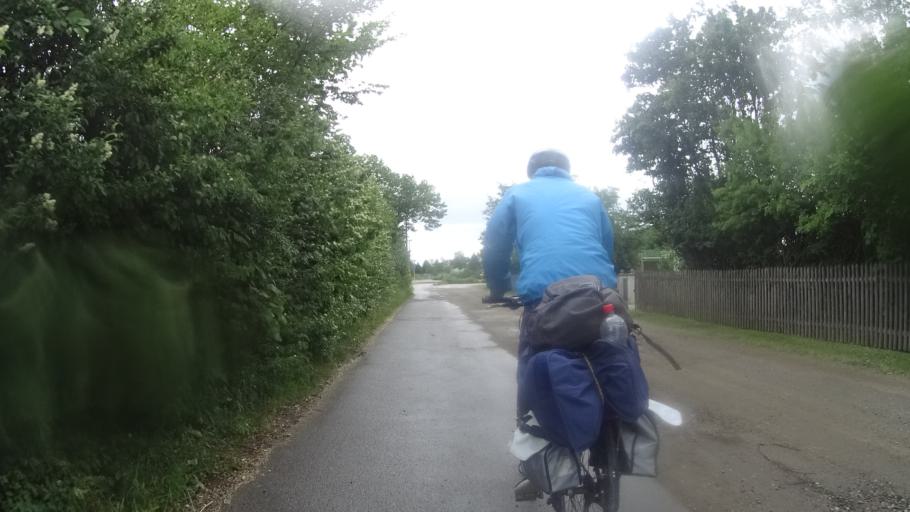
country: DE
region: Bavaria
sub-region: Upper Bavaria
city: Maisach
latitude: 48.2159
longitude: 11.2715
